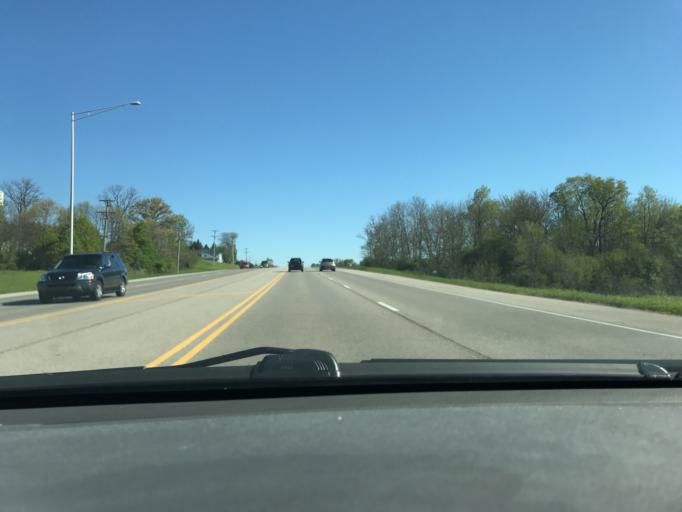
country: US
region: Illinois
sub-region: Kane County
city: Sleepy Hollow
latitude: 42.1091
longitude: -88.3350
